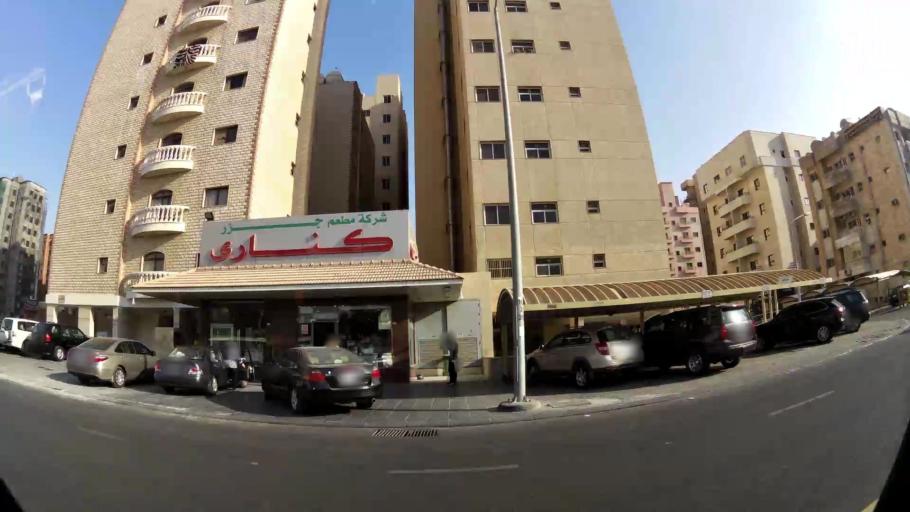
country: KW
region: Muhafazat Hawalli
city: As Salimiyah
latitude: 29.3362
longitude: 48.0864
